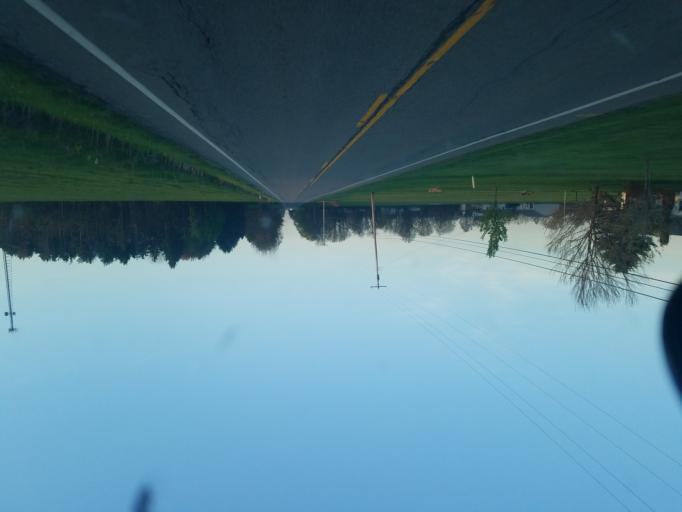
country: US
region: Ohio
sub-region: Trumbull County
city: Brookfield Center
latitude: 41.3003
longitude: -80.5685
